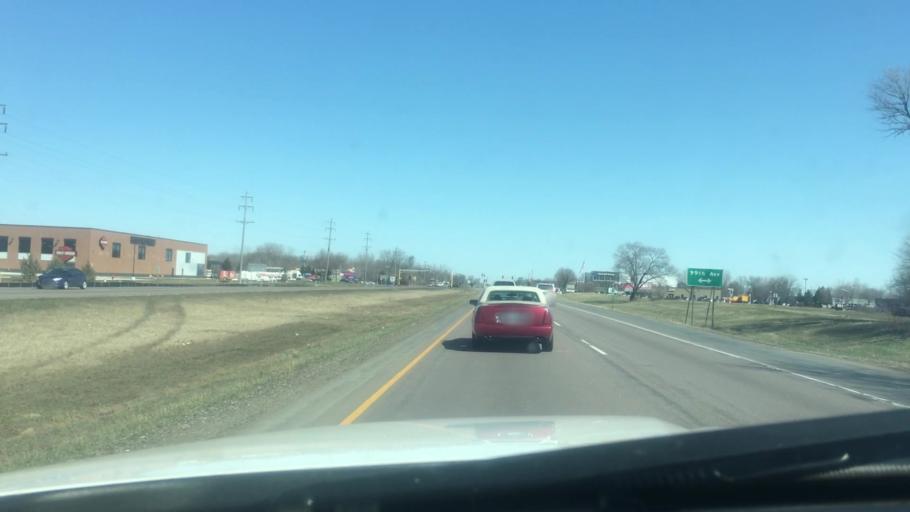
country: US
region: Minnesota
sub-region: Anoka County
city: Blaine
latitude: 45.1468
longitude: -93.2352
